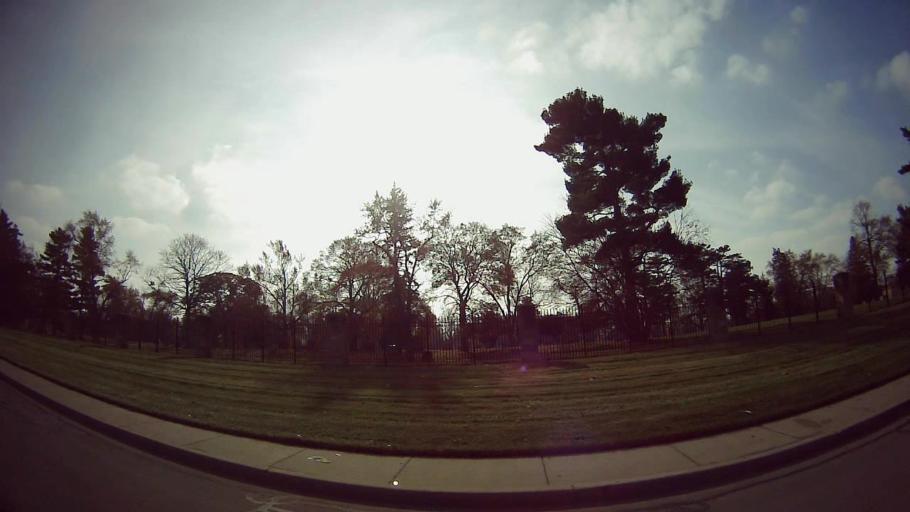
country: US
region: Michigan
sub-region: Wayne County
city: Redford
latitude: 42.4231
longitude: -83.2745
